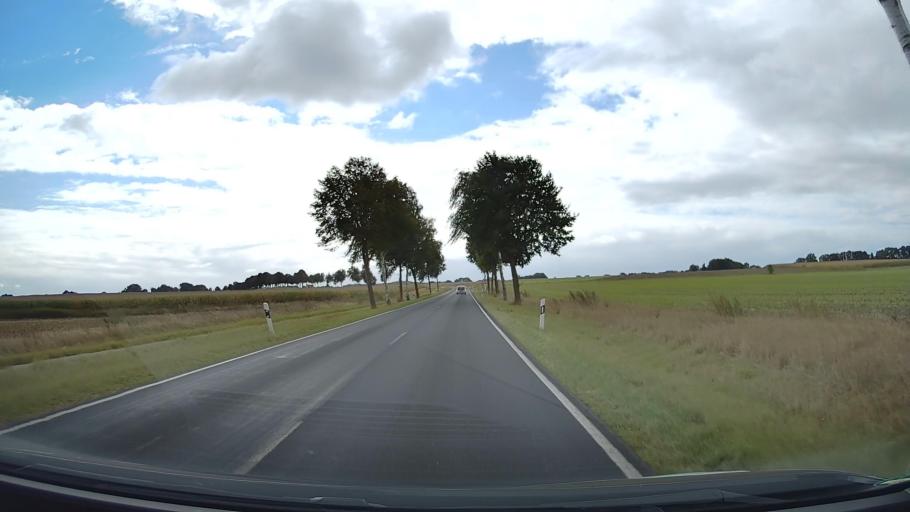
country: DE
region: Lower Saxony
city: Rhade
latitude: 53.3207
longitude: 9.1264
